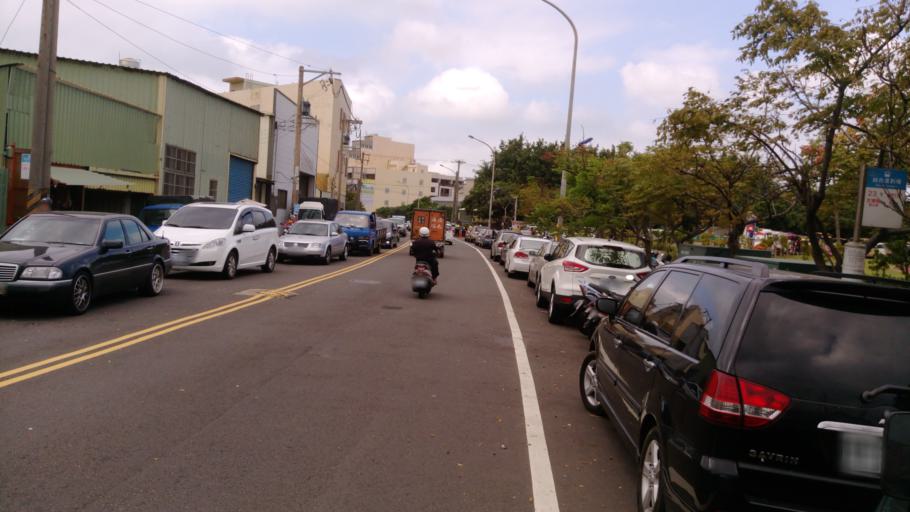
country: TW
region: Taiwan
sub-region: Hsinchu
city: Hsinchu
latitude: 24.7923
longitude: 120.9303
